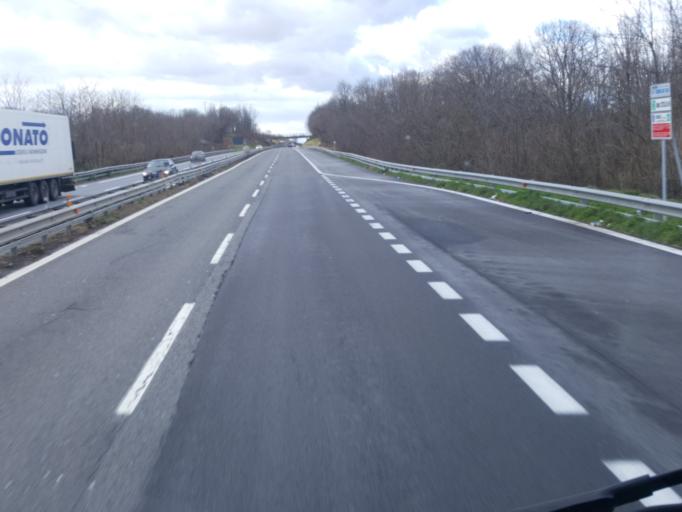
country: IT
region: Calabria
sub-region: Provincia di Cosenza
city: Santo Stefano di Rogliano
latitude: 39.2120
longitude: 16.3072
